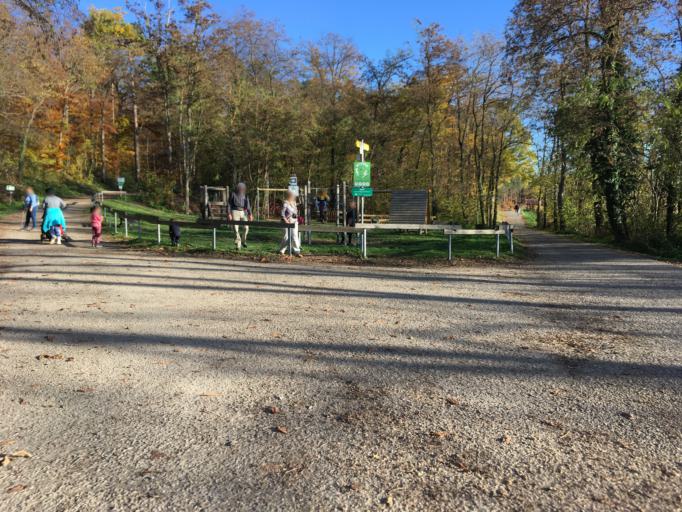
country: DE
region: Baden-Wuerttemberg
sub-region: Karlsruhe Region
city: Oberderdingen
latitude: 49.0453
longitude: 8.8035
